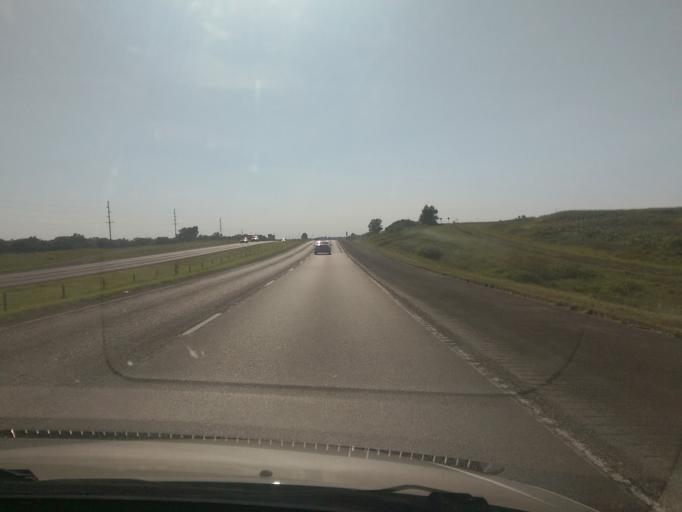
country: US
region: Missouri
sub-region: Lafayette County
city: Higginsville
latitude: 38.9927
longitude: -93.6912
